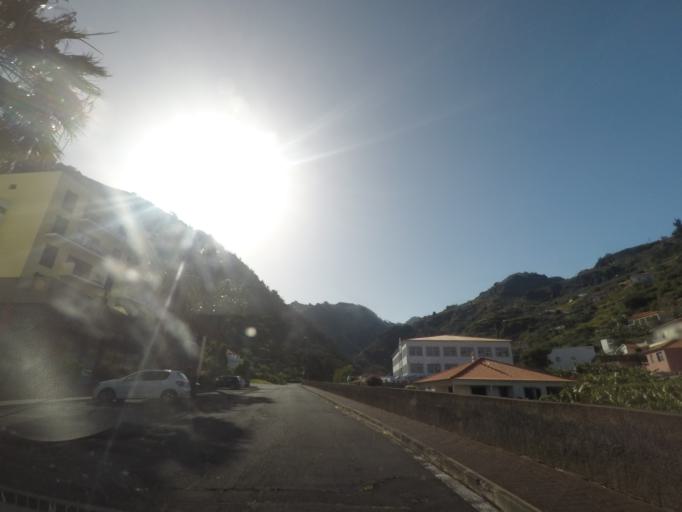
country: PT
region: Madeira
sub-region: Santa Cruz
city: Santa Cruz
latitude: 32.6899
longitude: -16.7965
